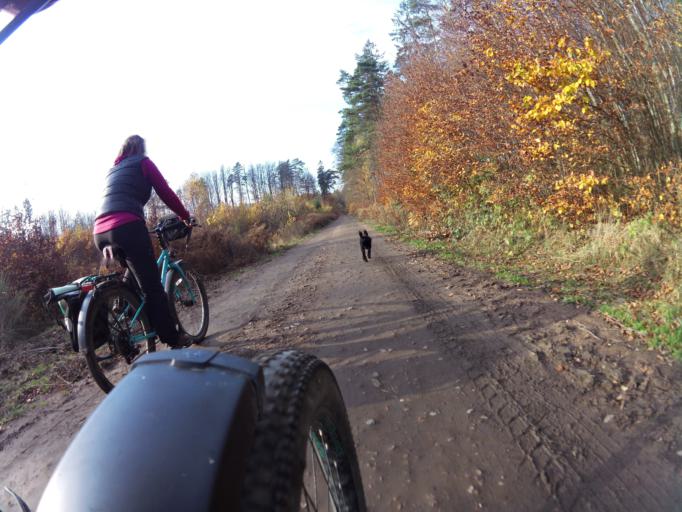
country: PL
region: Pomeranian Voivodeship
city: Strzelno
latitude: 54.7395
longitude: 18.2648
